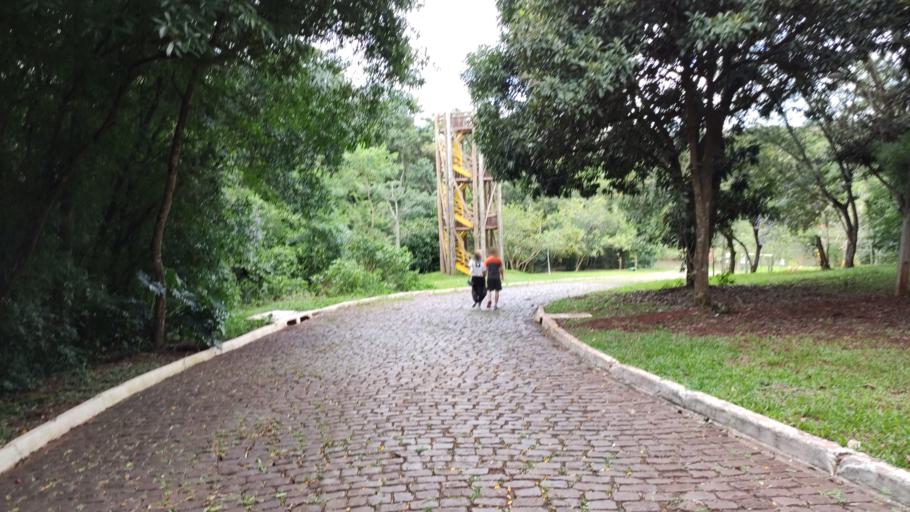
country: BR
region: Parana
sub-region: Londrina
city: Londrina
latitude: -23.3453
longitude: -51.1419
